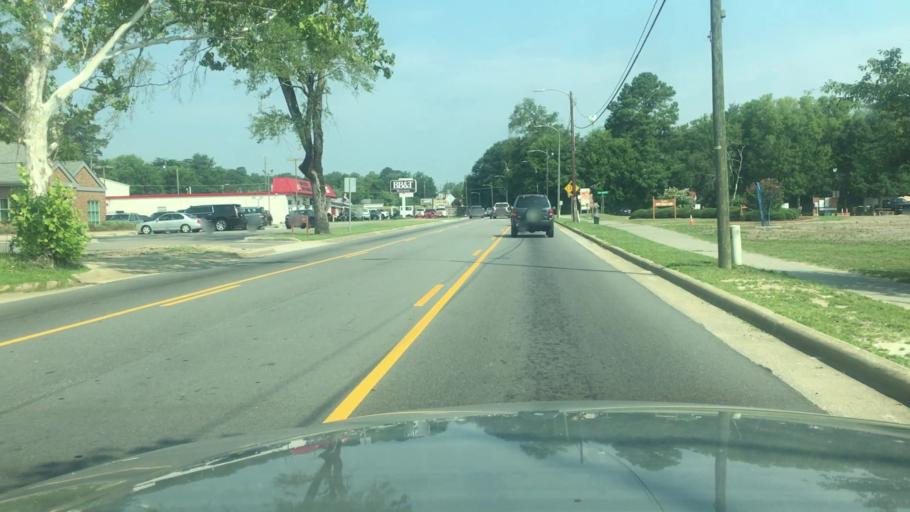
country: US
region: North Carolina
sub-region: Cumberland County
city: Hope Mills
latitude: 34.9730
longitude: -78.9468
